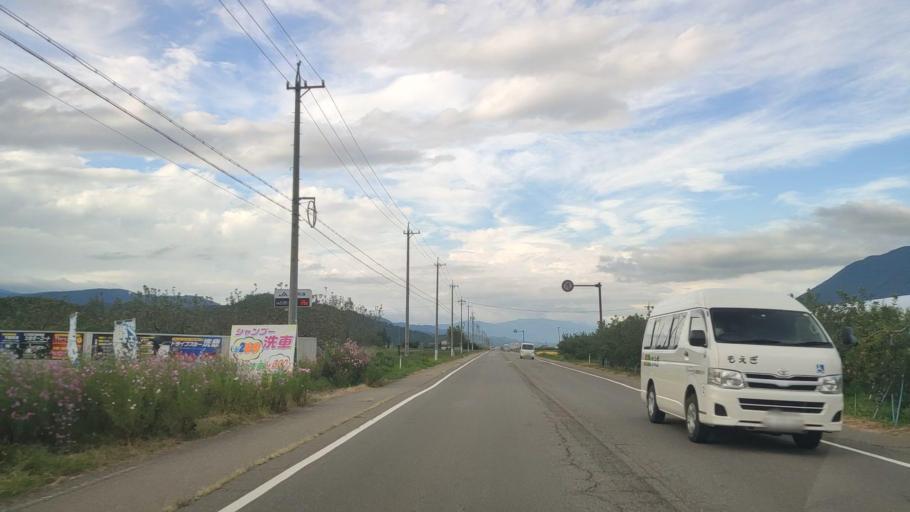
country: JP
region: Nagano
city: Nakano
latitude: 36.7692
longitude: 138.3505
